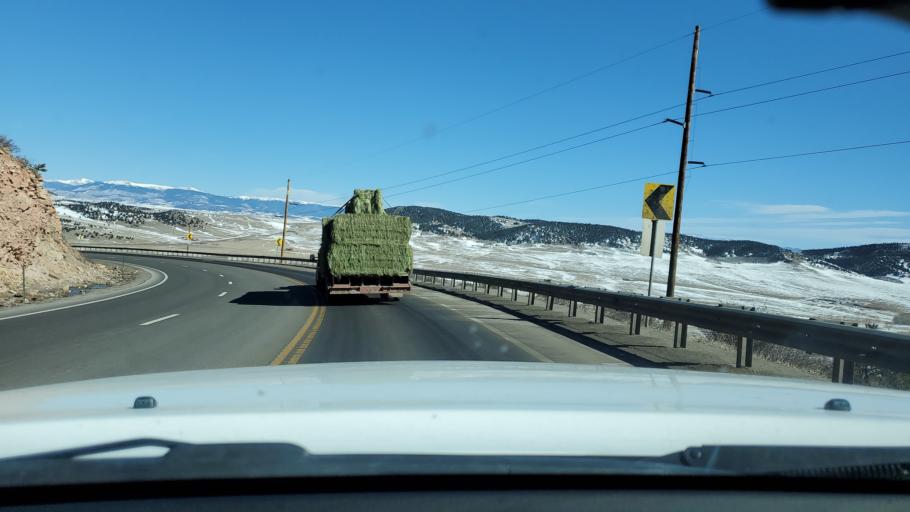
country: US
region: Colorado
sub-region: Park County
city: Fairplay
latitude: 39.2643
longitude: -105.9593
